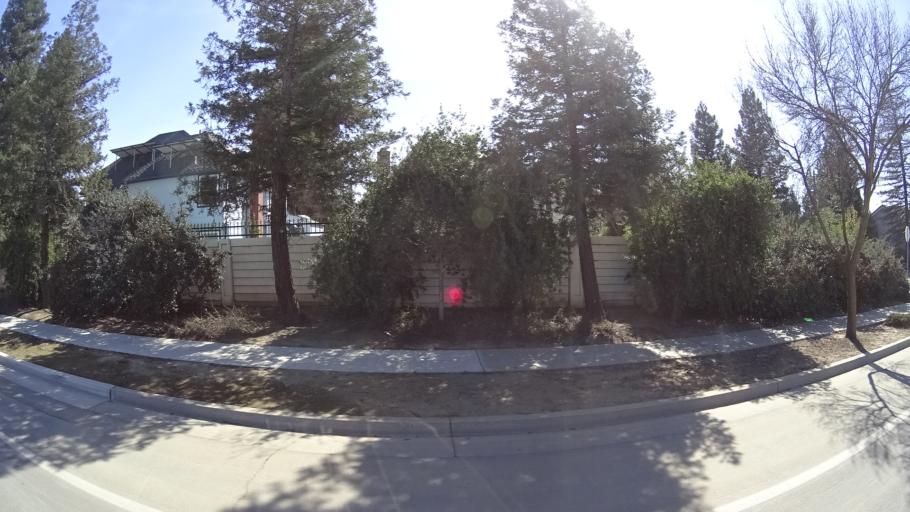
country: US
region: California
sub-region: Fresno County
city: Clovis
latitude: 36.8448
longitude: -119.7431
